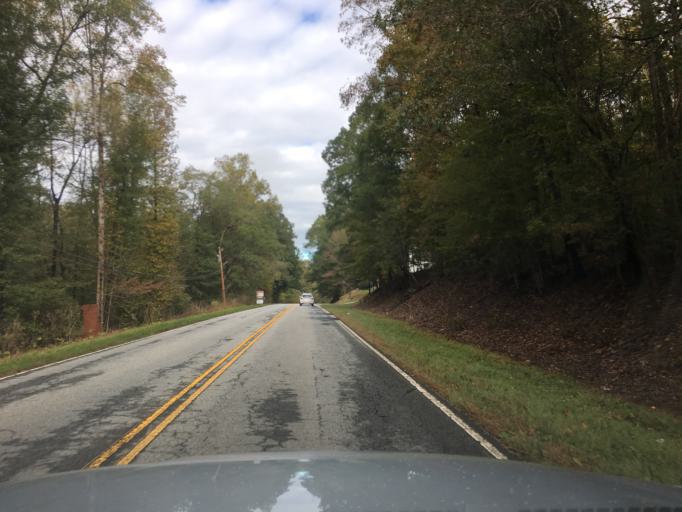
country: US
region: South Carolina
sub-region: Greenville County
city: Greer
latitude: 35.0184
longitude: -82.2648
